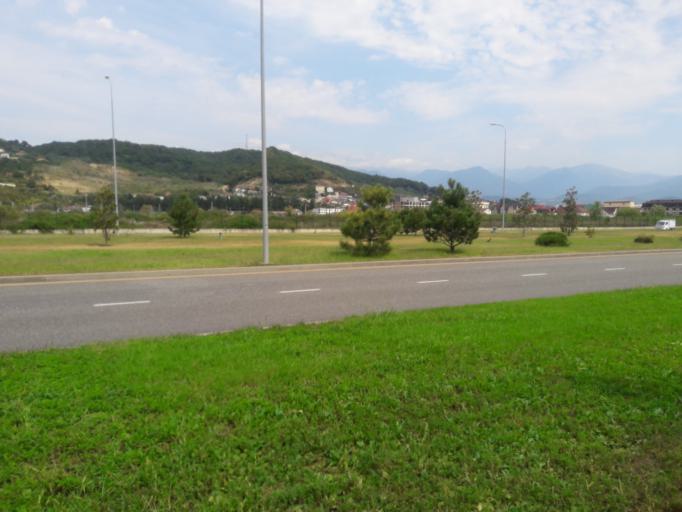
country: RU
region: Krasnodarskiy
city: Adler
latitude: 43.4048
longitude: 39.9767
